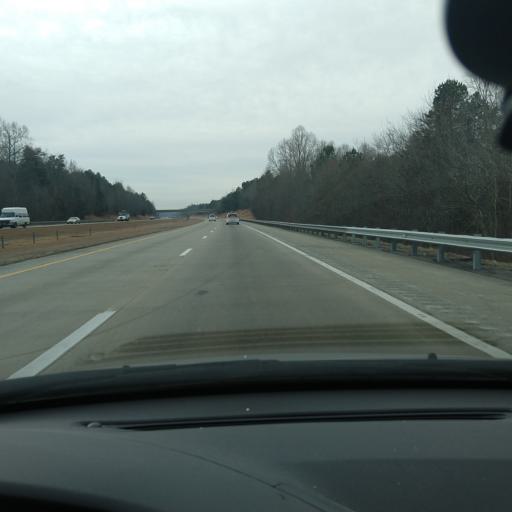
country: US
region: North Carolina
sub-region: Davidson County
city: Welcome
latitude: 35.9065
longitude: -80.2349
